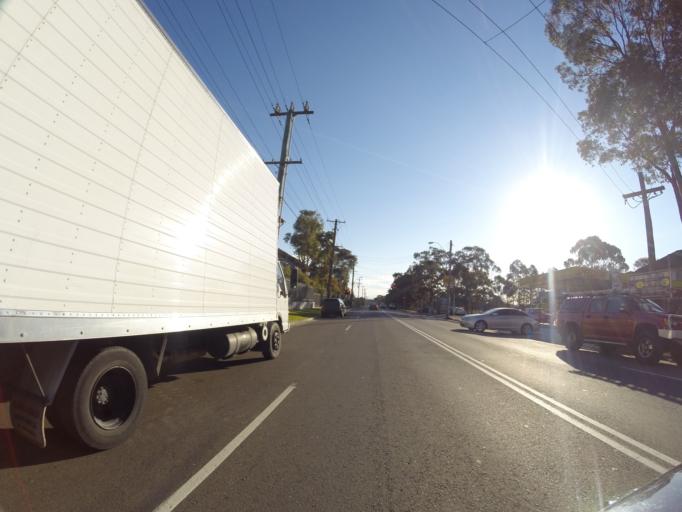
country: AU
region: New South Wales
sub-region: Fairfield
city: Fairfield East
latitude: -33.8700
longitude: 150.9810
